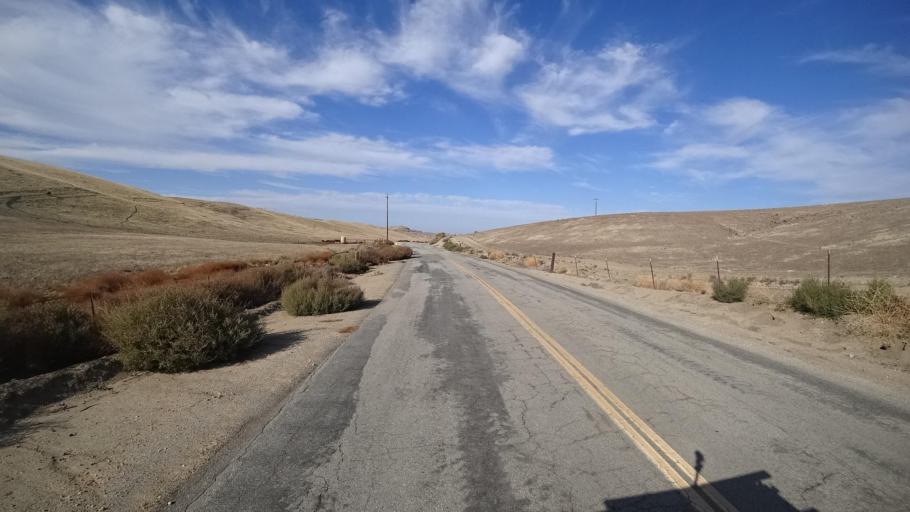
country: US
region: California
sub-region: Kern County
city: Oildale
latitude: 35.6067
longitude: -118.9577
